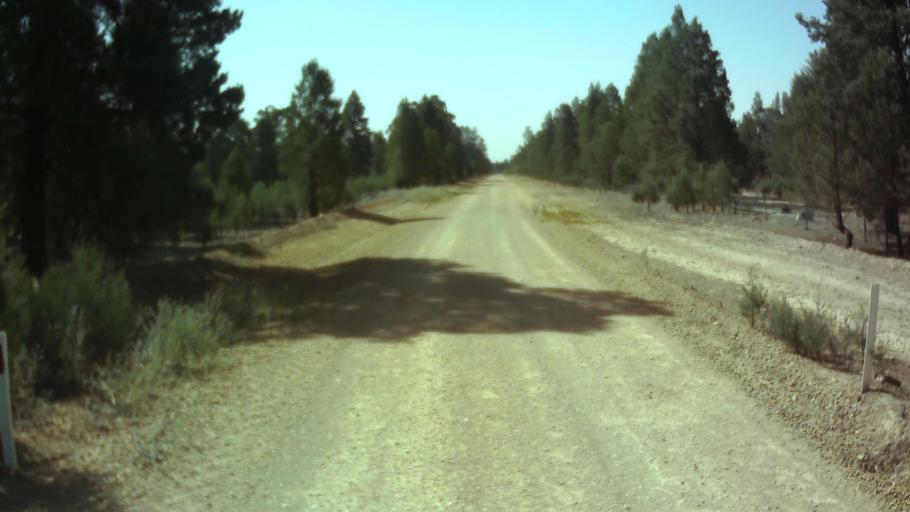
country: AU
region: New South Wales
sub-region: Weddin
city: Grenfell
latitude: -33.9170
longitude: 147.9224
